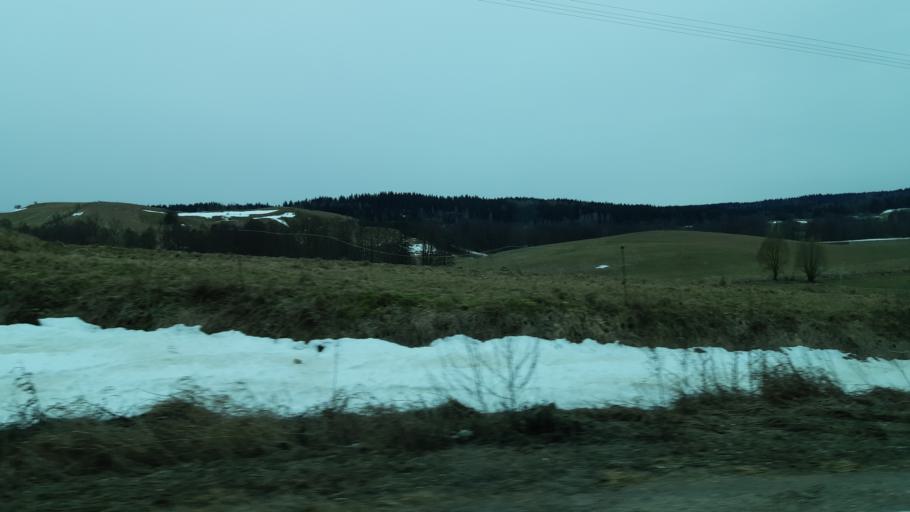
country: PL
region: Podlasie
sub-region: Suwalki
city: Suwalki
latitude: 54.3343
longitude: 22.9330
